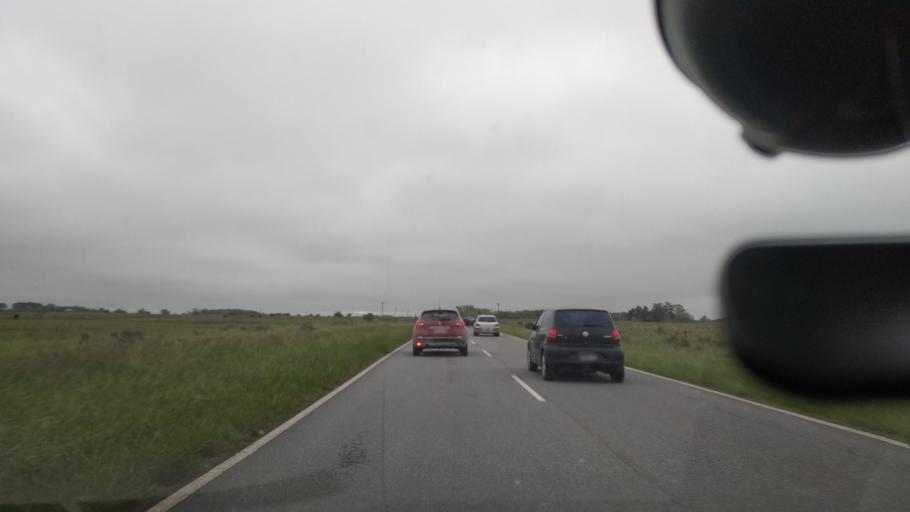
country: AR
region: Buenos Aires
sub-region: Partido de Magdalena
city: Magdalena
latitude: -35.2453
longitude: -57.6768
